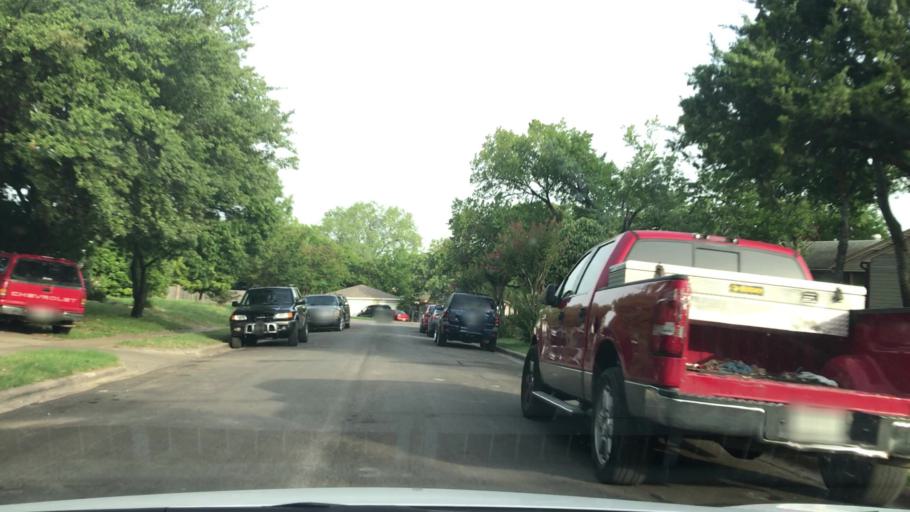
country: US
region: Texas
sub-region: Dallas County
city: Dallas
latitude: 32.7777
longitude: -96.7123
